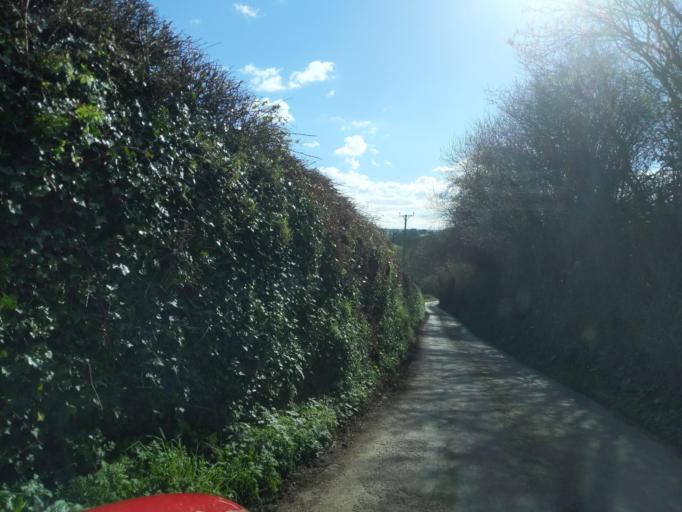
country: GB
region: England
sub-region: Devon
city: Kingsbridge
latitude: 50.2874
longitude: -3.7546
